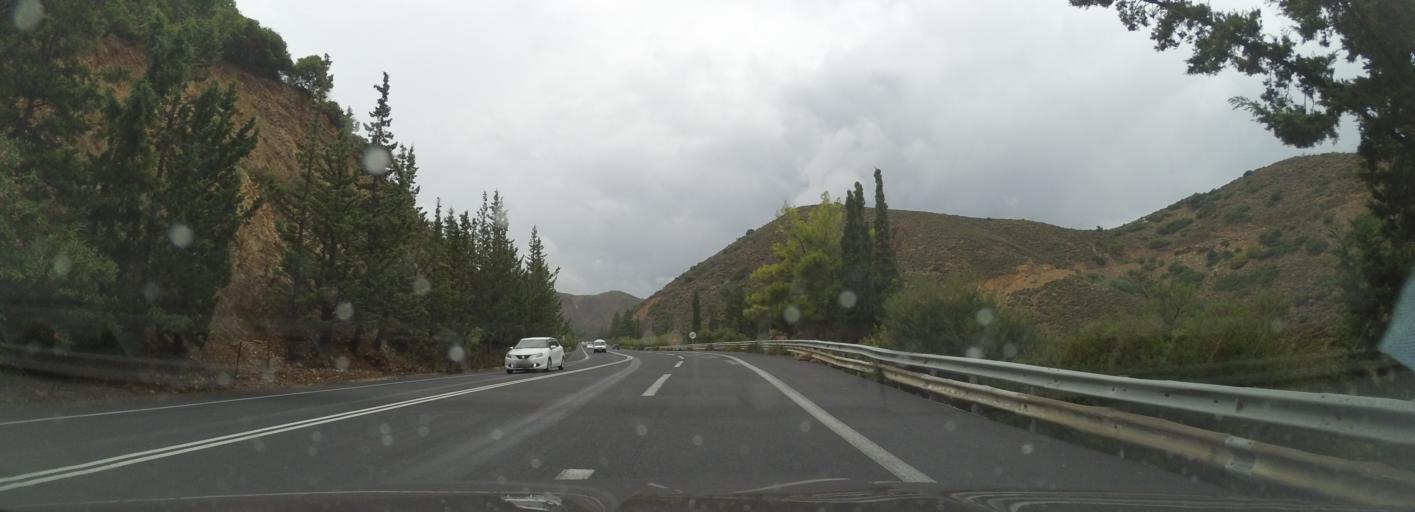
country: GR
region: Crete
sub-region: Nomos Rethymnis
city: Anogeia
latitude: 35.3898
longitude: 24.9443
